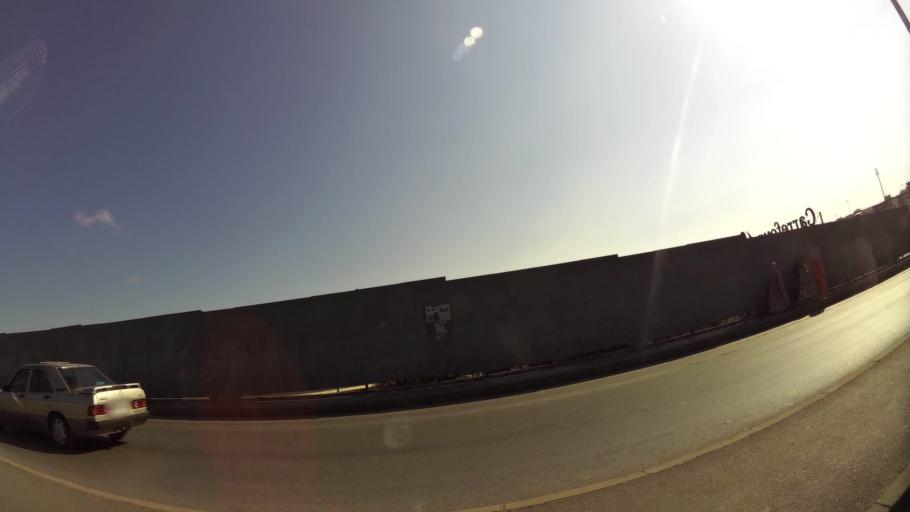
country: MA
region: Rabat-Sale-Zemmour-Zaer
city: Sale
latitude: 34.0592
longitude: -6.8010
